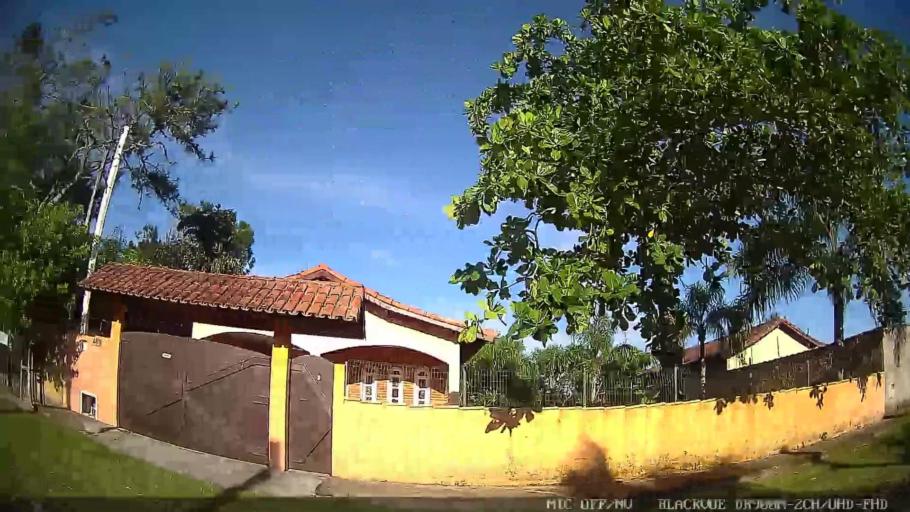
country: BR
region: Sao Paulo
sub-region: Iguape
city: Iguape
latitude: -24.7564
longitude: -47.5715
